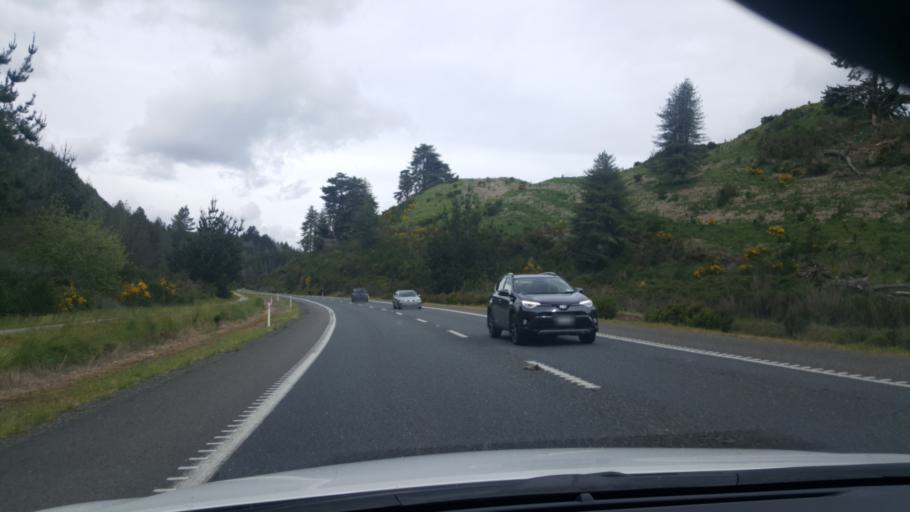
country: NZ
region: Bay of Plenty
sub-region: Rotorua District
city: Rotorua
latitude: -38.2140
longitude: 176.2653
